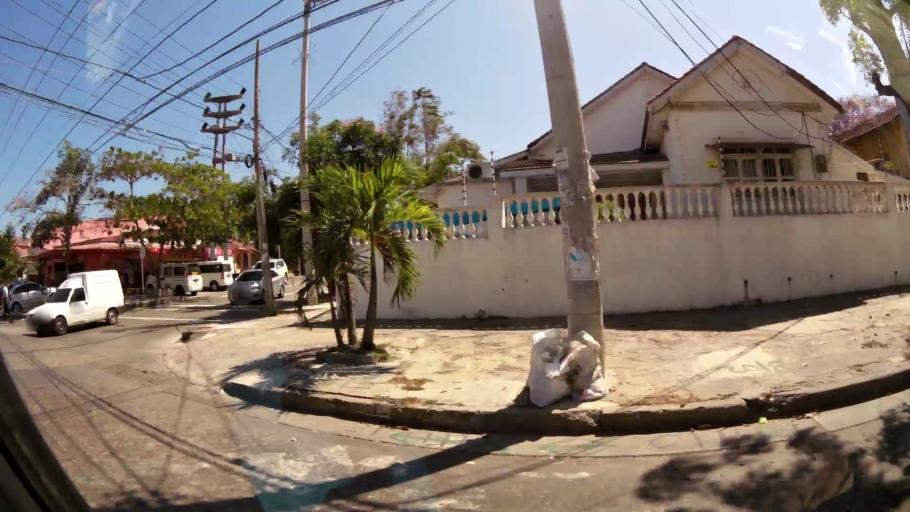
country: CO
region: Atlantico
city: Barranquilla
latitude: 10.9970
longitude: -74.7929
